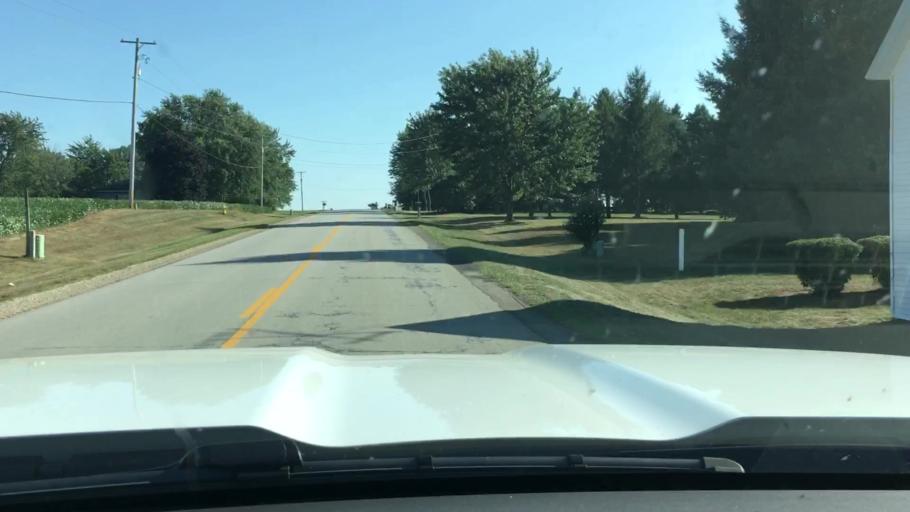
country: US
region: Michigan
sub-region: Ottawa County
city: Zeeland
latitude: 42.8540
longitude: -85.9600
